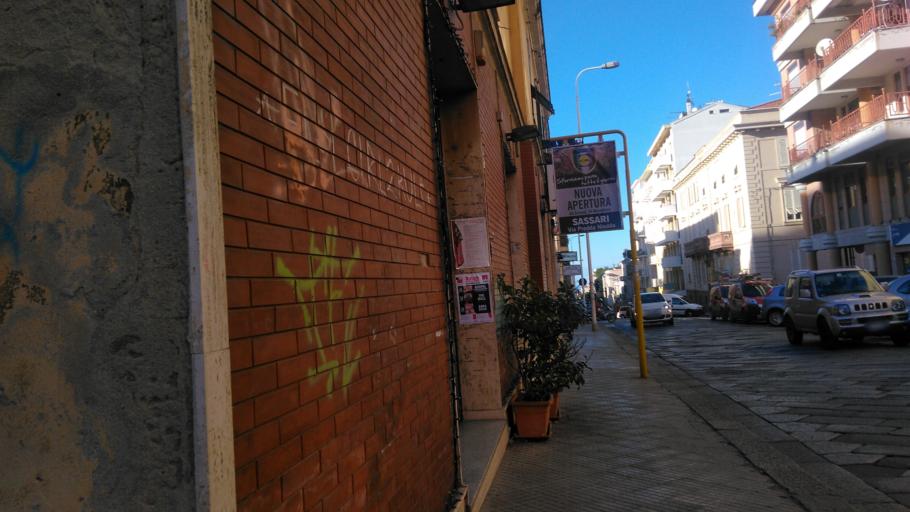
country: IT
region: Sardinia
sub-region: Provincia di Sassari
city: Sassari
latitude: 40.7194
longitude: 8.5701
